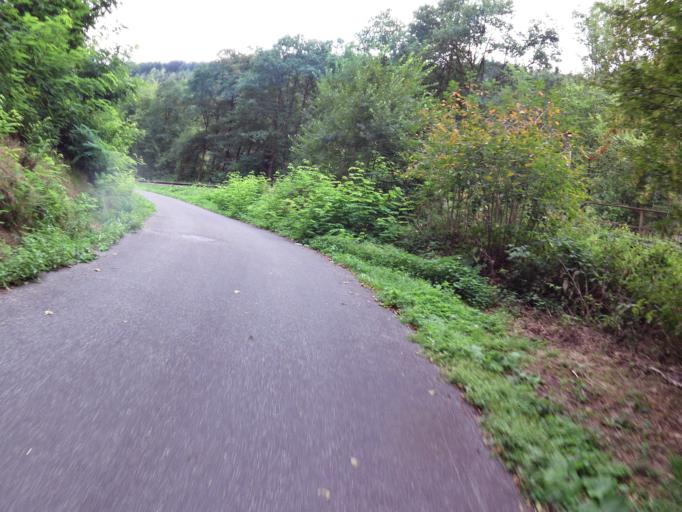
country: DE
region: Rheinland-Pfalz
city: Sankt Thomas
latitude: 50.0525
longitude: 6.5986
